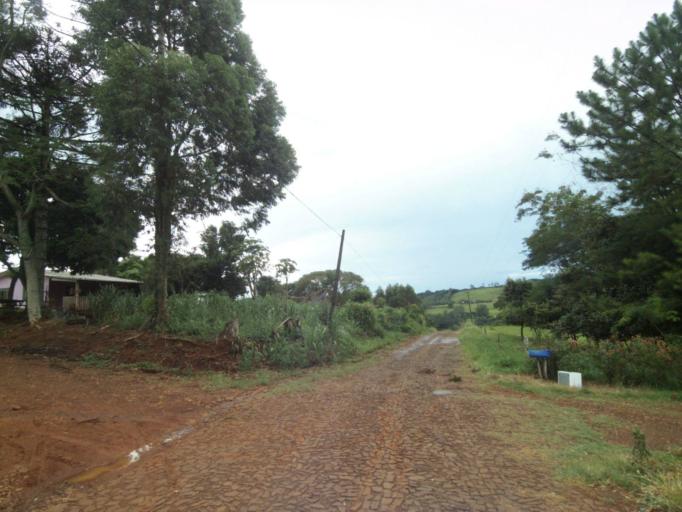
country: BR
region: Parana
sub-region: Guaraniacu
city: Guaraniacu
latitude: -25.0937
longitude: -52.8655
